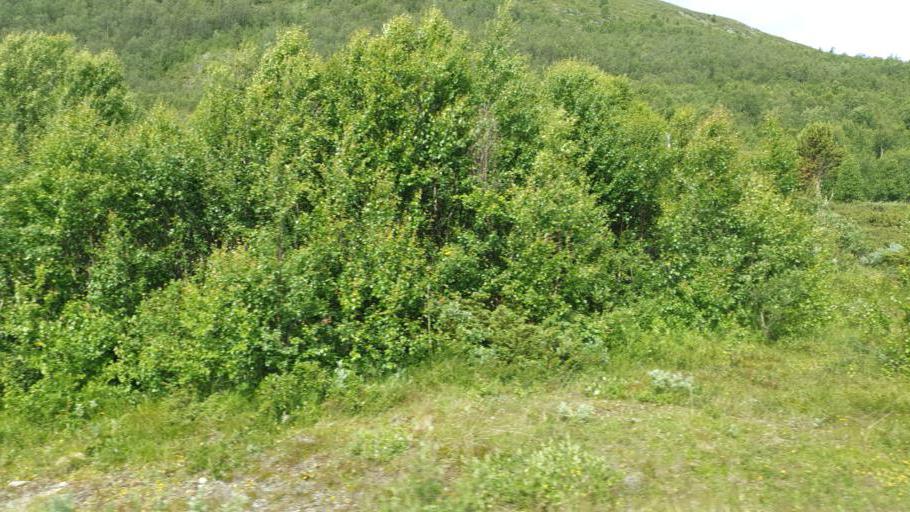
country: NO
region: Oppland
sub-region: Vaga
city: Vagamo
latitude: 61.5268
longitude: 8.8754
